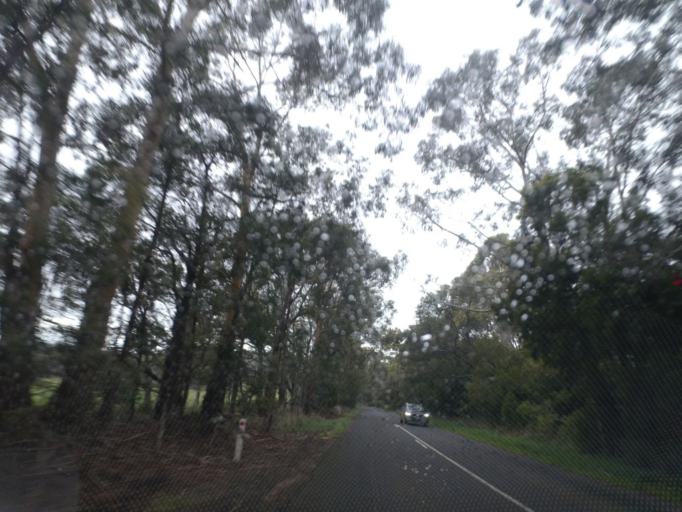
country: AU
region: Victoria
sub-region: Hume
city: Sunbury
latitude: -37.3525
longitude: 144.6462
